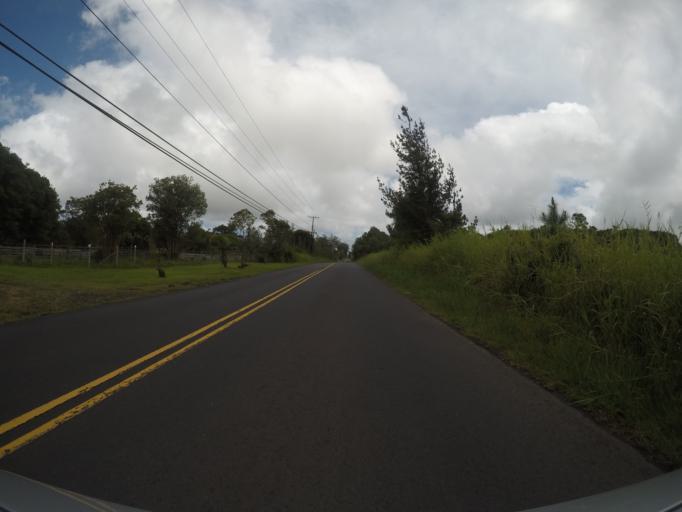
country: US
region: Hawaii
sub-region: Hawaii County
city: Fern Acres
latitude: 19.4840
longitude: -155.1492
